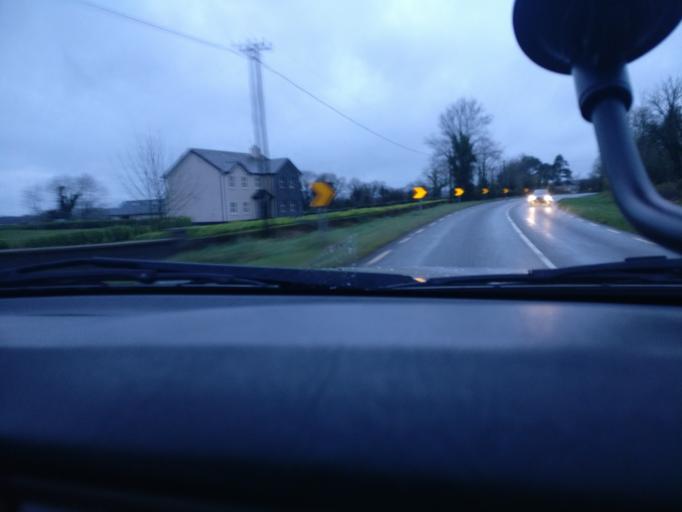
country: IE
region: Connaught
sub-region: County Galway
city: Ballinasloe
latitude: 53.2707
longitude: -8.3866
